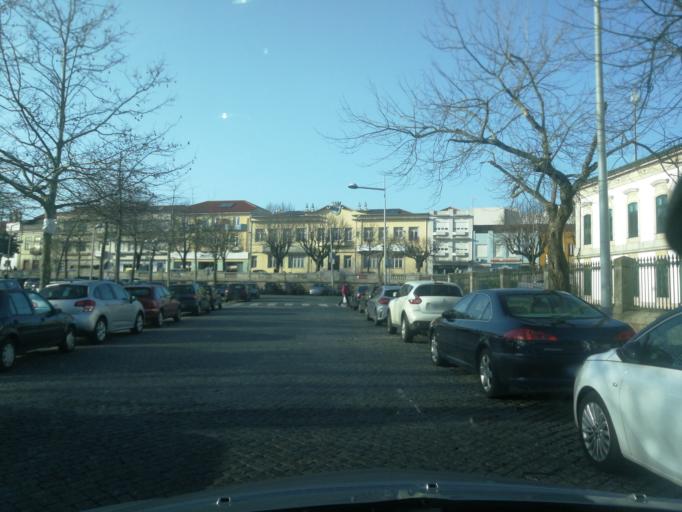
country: PT
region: Braga
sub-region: Barcelos
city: Barcelos
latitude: 41.5332
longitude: -8.6172
